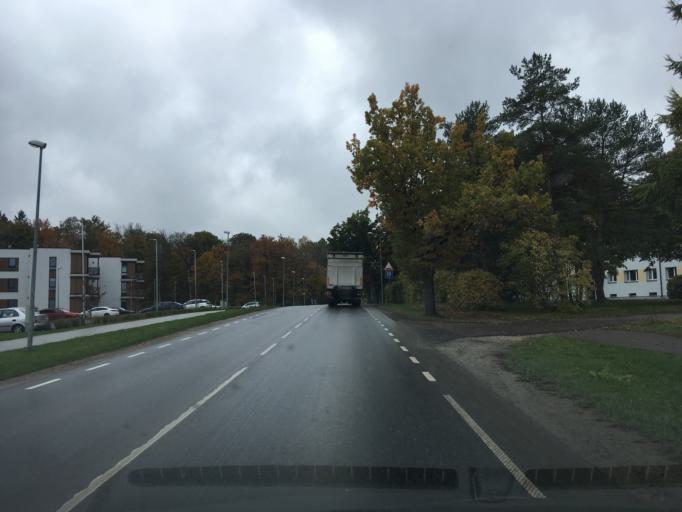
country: EE
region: Harju
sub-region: Saue vald
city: Laagri
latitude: 59.3883
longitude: 24.5786
